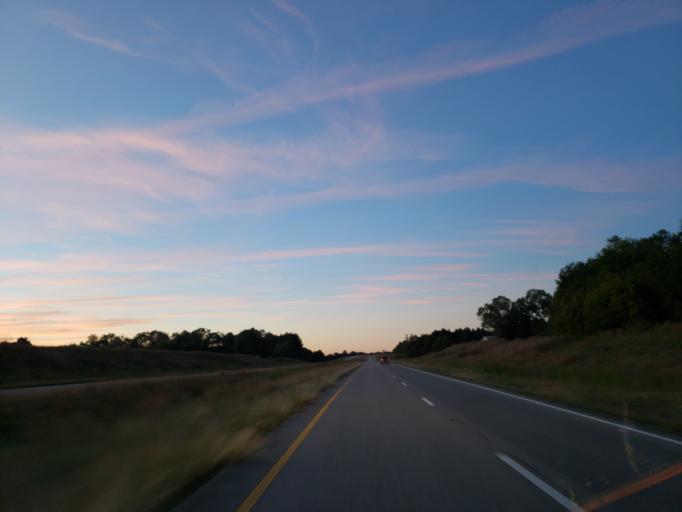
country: US
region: Mississippi
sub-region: Wayne County
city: Waynesboro
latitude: 31.7631
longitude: -88.6688
